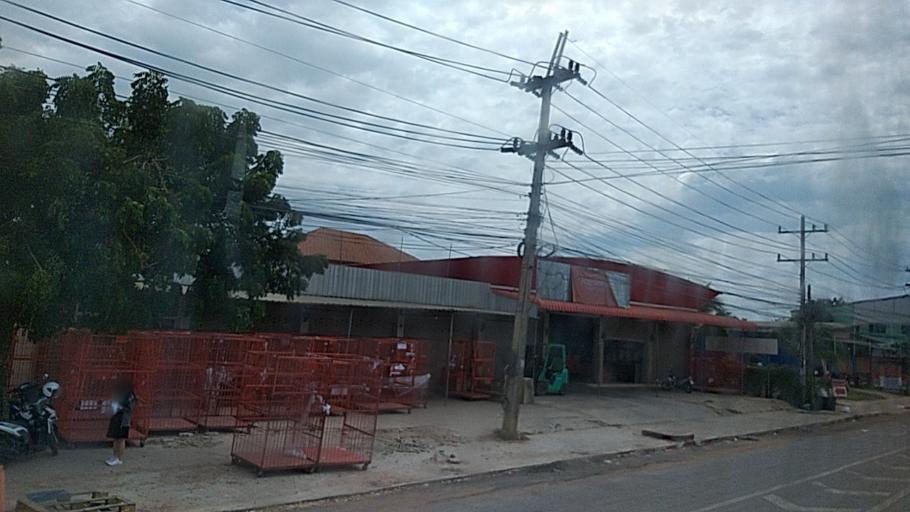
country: TH
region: Maha Sarakham
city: Maha Sarakham
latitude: 16.2297
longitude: 103.2712
